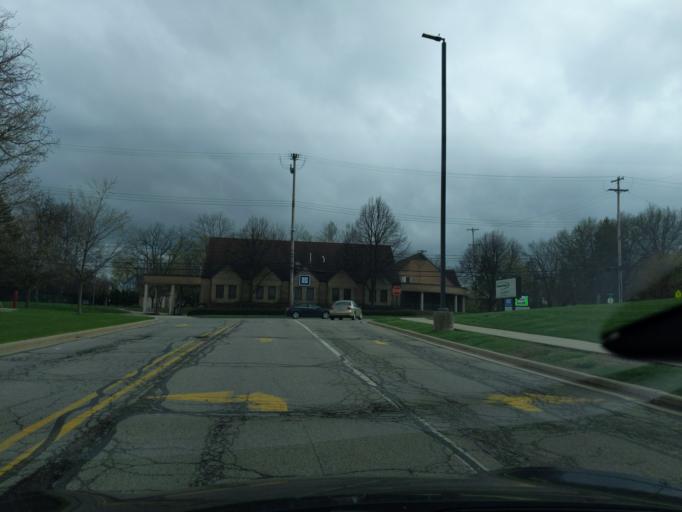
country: US
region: Michigan
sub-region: Ingham County
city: Lansing
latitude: 42.7492
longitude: -84.5593
